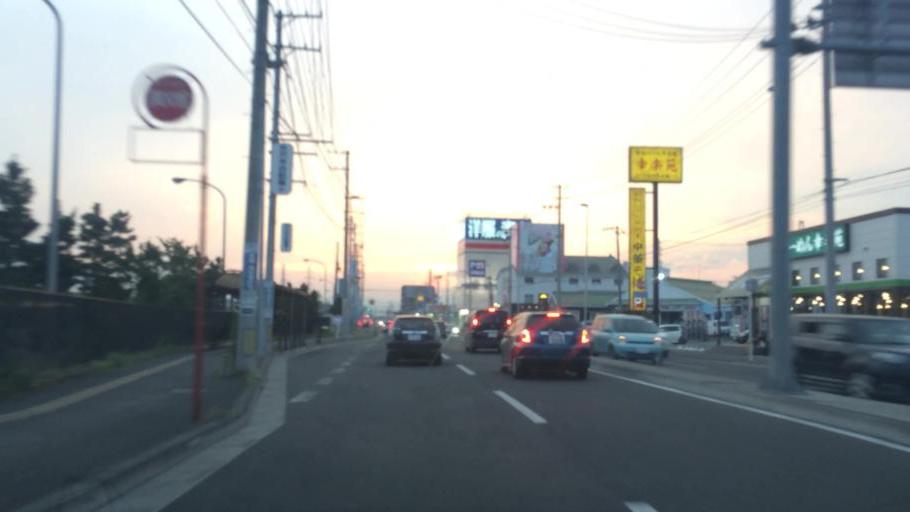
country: JP
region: Miyagi
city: Sendai-shi
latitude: 38.3140
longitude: 140.9065
